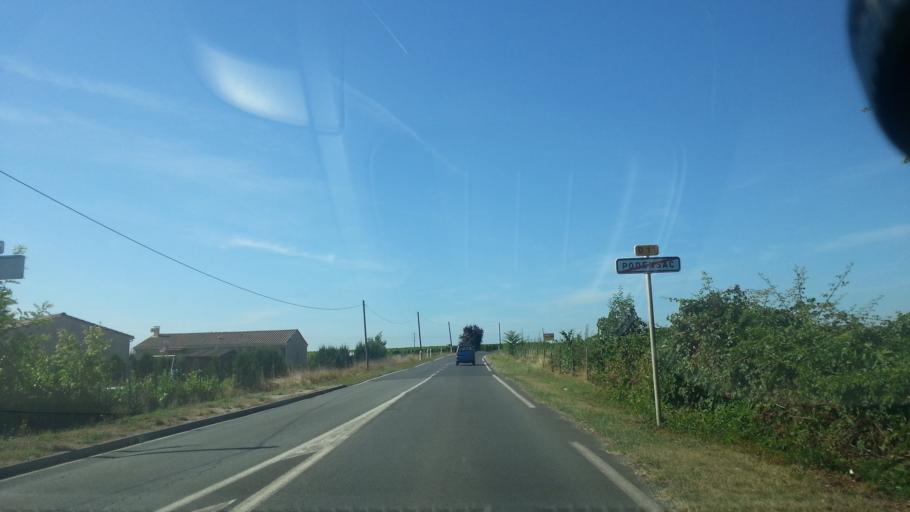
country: FR
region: Aquitaine
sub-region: Departement de la Gironde
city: Podensac
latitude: 44.6437
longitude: -0.3591
